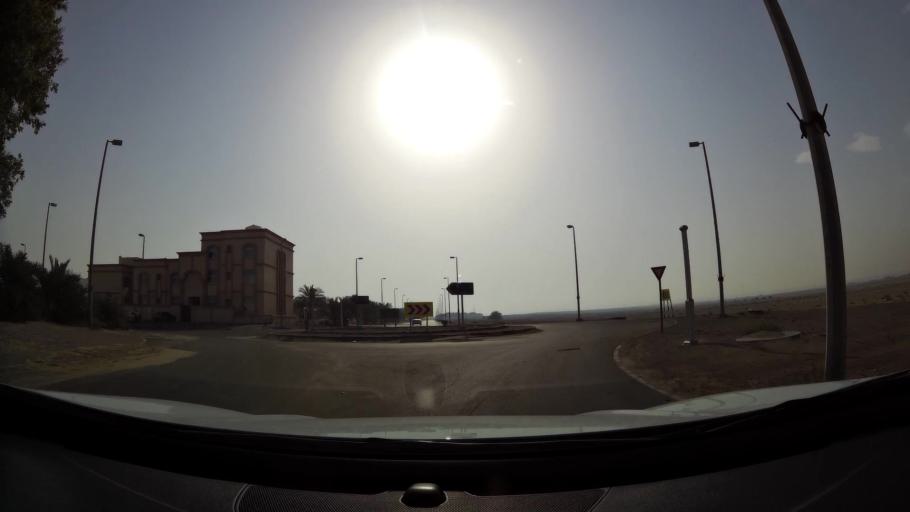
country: AE
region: Abu Dhabi
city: Abu Dhabi
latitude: 24.2615
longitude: 54.6648
